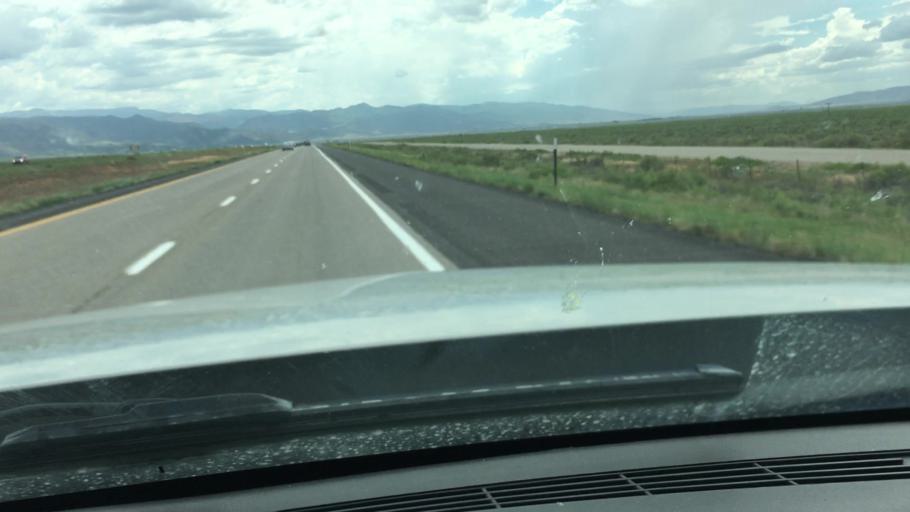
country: US
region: Utah
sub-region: Iron County
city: Parowan
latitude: 37.9683
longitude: -112.7449
